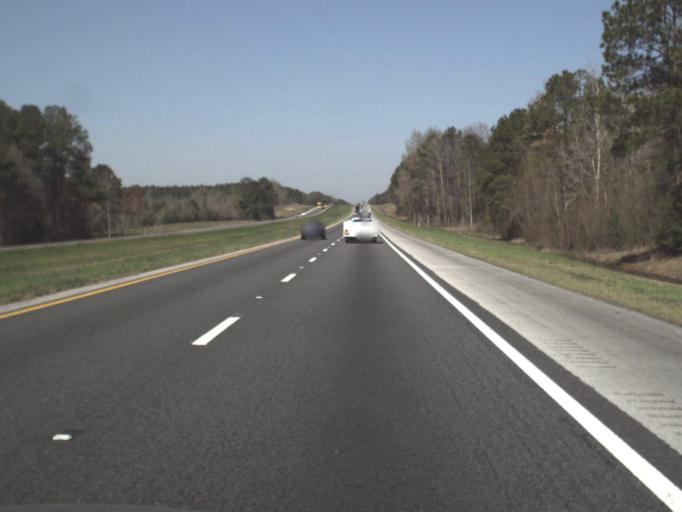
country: US
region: Florida
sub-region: Jackson County
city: Marianna
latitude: 30.6894
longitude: -85.1155
